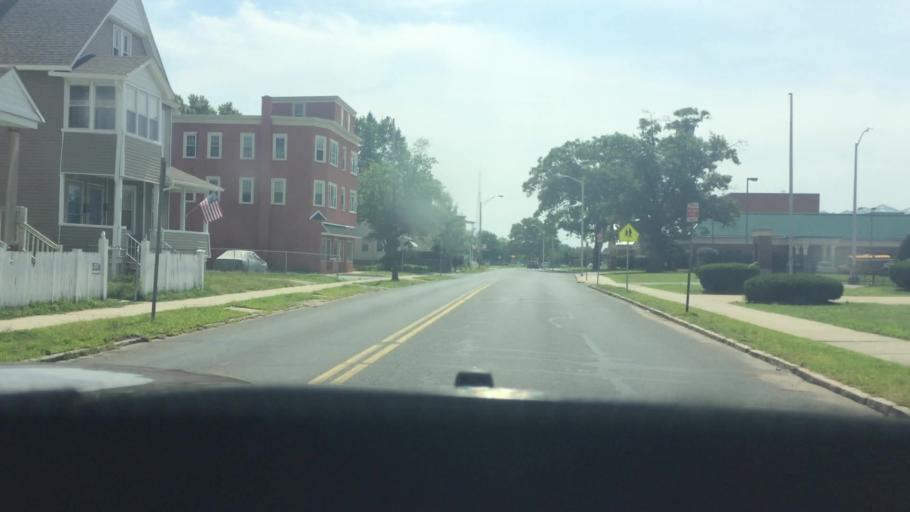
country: US
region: Massachusetts
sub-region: Hampden County
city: Springfield
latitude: 42.1215
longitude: -72.5878
